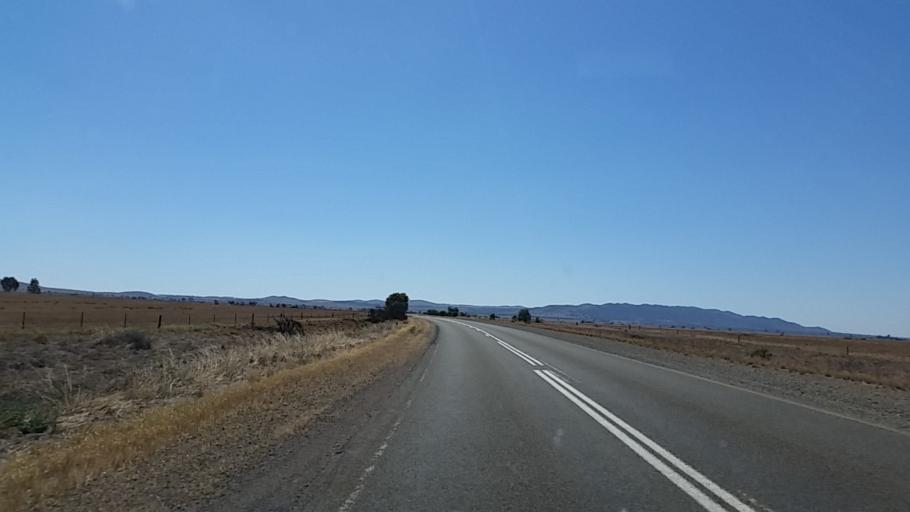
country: AU
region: South Australia
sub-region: Peterborough
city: Peterborough
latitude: -32.6672
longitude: 138.6075
